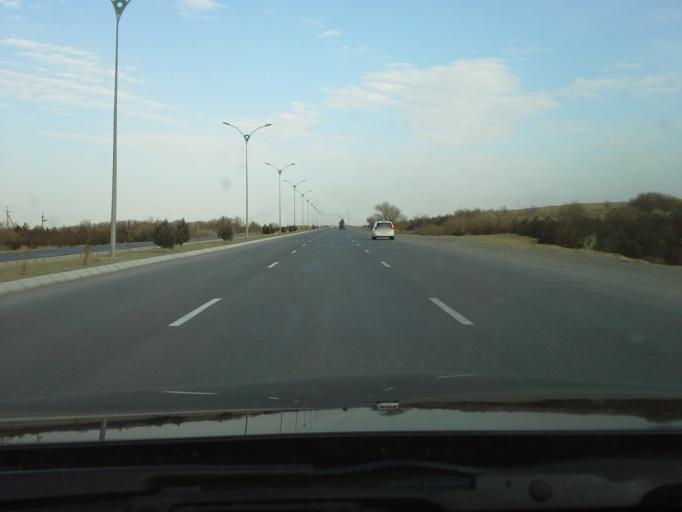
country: TM
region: Ahal
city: Abadan
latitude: 38.1041
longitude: 58.3261
